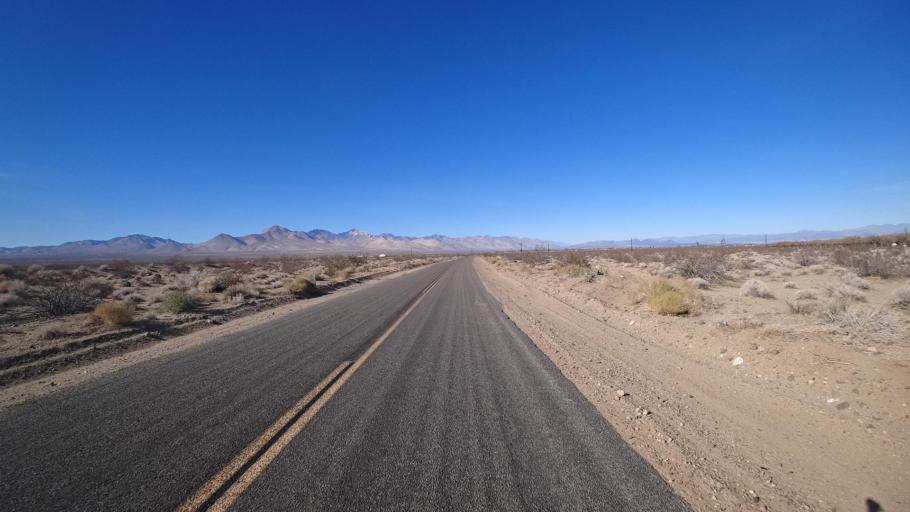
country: US
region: California
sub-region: Kern County
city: China Lake Acres
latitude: 35.5899
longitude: -117.7930
